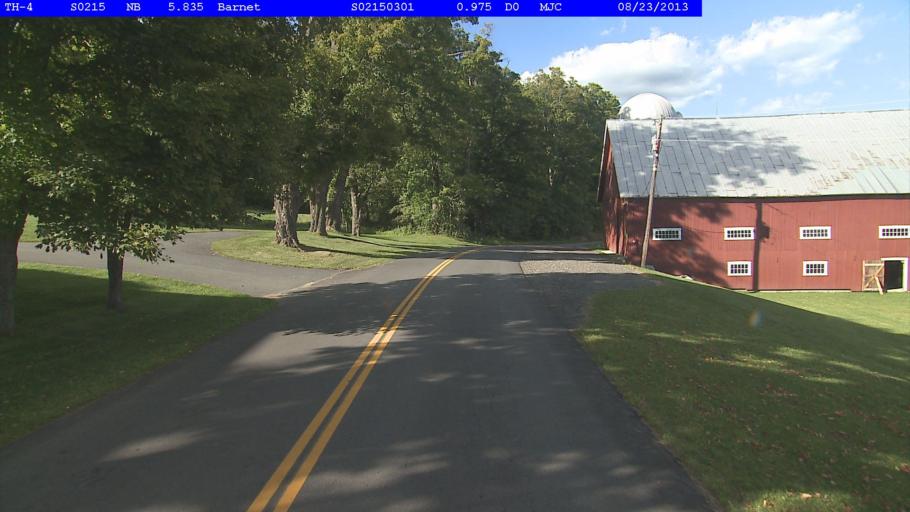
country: US
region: New Hampshire
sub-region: Grafton County
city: Woodsville
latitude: 44.2880
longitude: -72.1695
